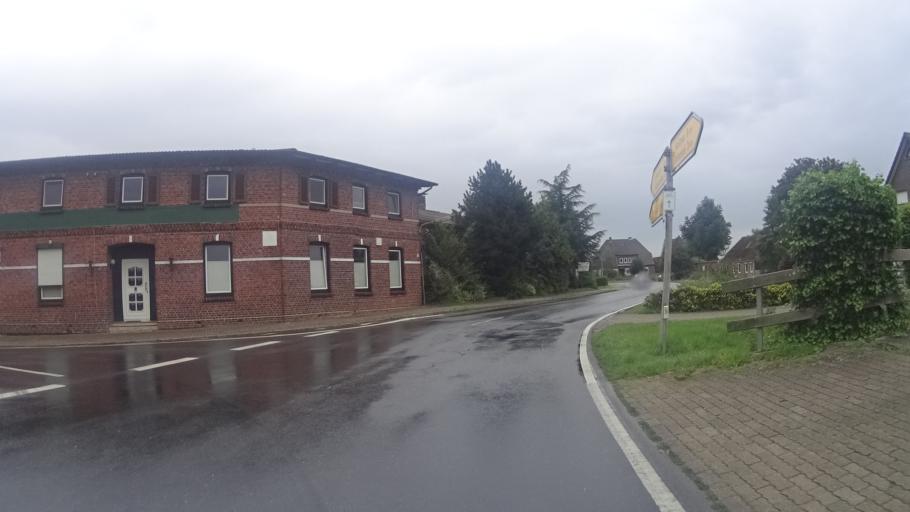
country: DE
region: Schleswig-Holstein
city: Altenmoor
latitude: 53.7875
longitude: 9.5723
